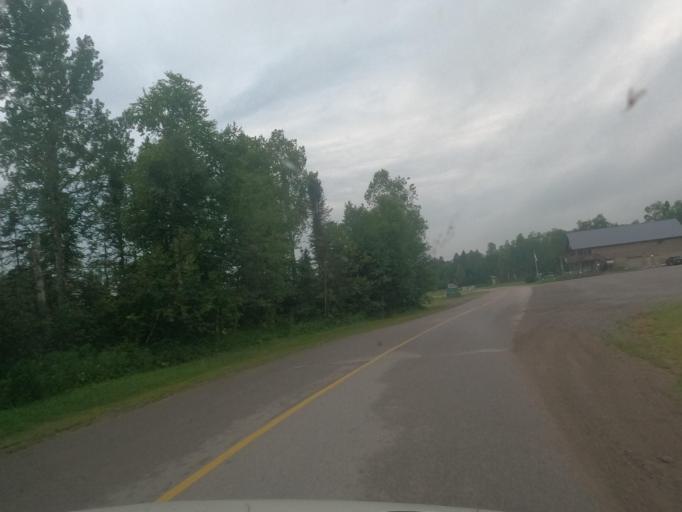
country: CA
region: Ontario
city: Marathon
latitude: 48.7774
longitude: -87.1083
